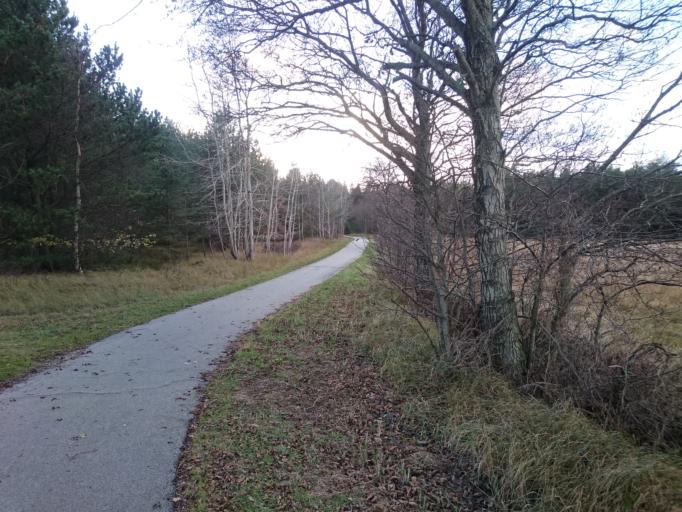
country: DK
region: North Denmark
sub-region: Frederikshavn Kommune
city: Skagen
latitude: 57.7053
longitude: 10.5244
